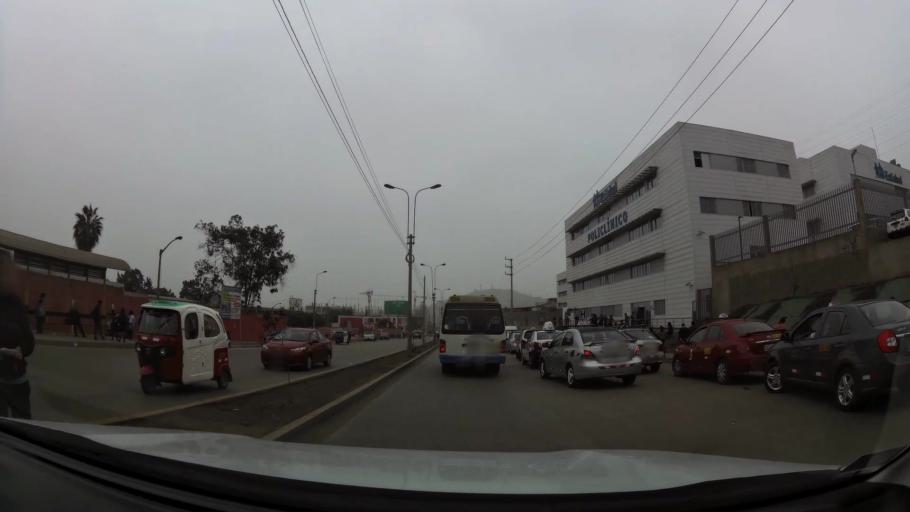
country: PE
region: Lima
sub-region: Lima
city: Surco
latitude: -12.1777
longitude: -76.9397
